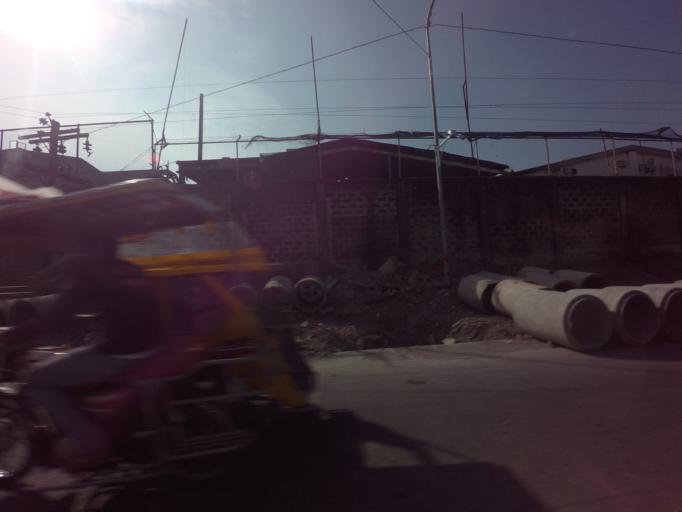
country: PH
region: Calabarzon
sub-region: Province of Rizal
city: Taguig
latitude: 14.5009
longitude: 121.0479
